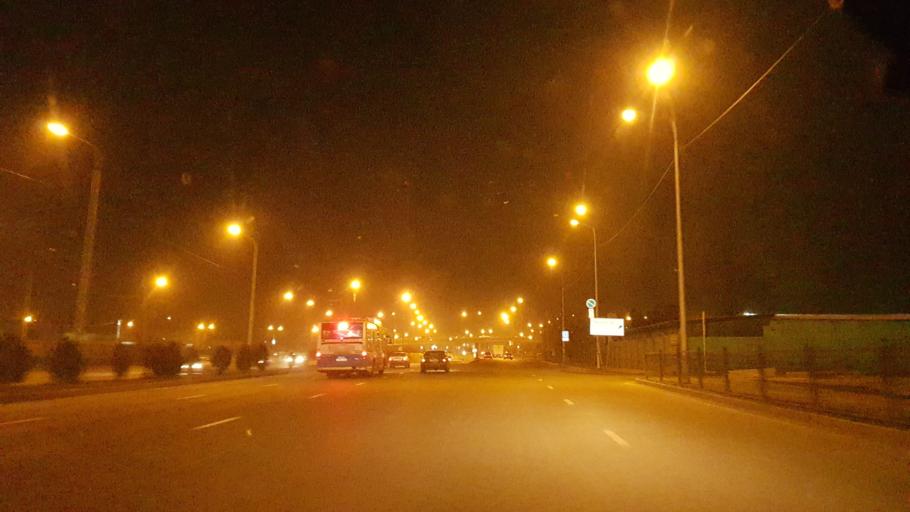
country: KZ
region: Almaty Qalasy
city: Almaty
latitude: 43.2752
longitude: 76.8864
